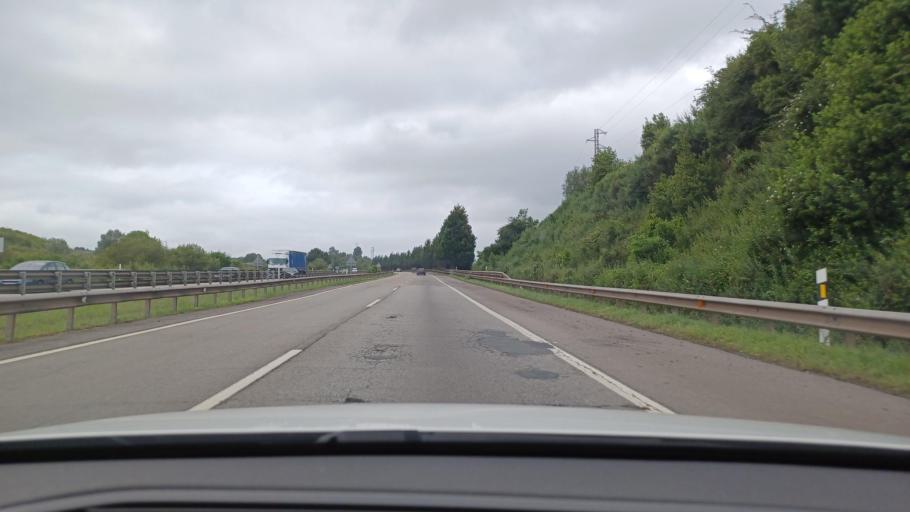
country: ES
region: Asturias
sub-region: Province of Asturias
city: Natahoyo
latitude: 43.5150
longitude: -5.7297
